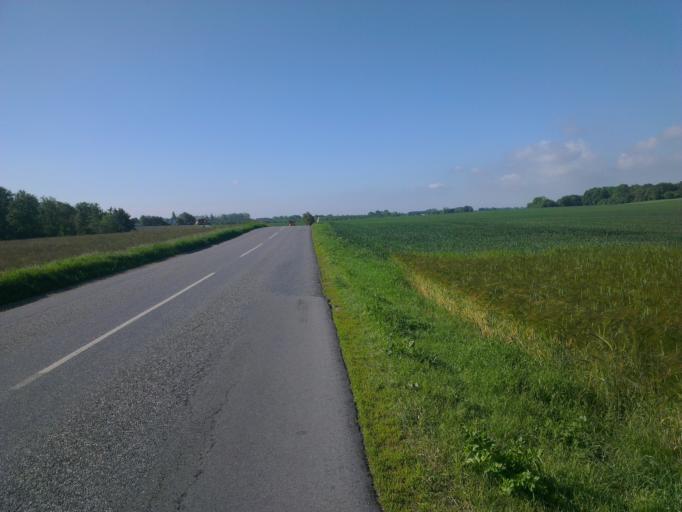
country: DK
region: Capital Region
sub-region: Frederikssund Kommune
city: Skibby
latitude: 55.7911
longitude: 12.0115
